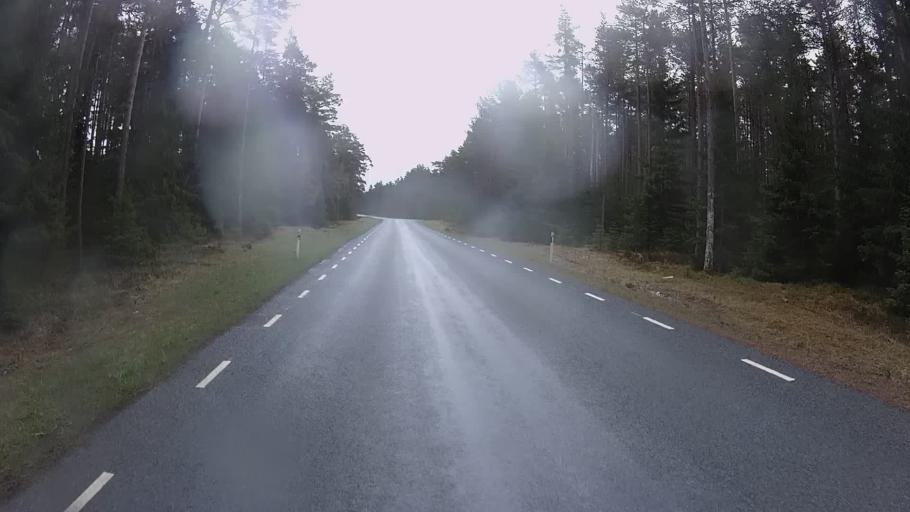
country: EE
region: Hiiumaa
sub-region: Kaerdla linn
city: Kardla
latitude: 58.9117
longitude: 22.3879
